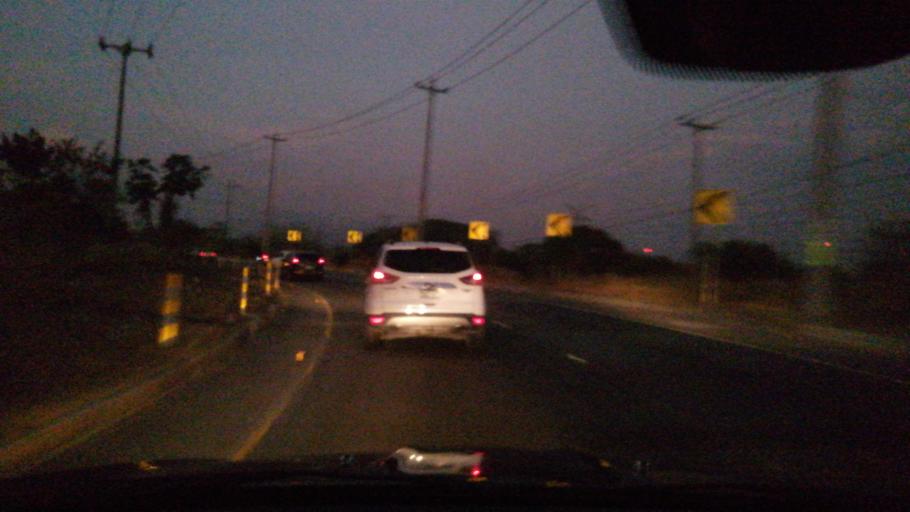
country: SV
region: San Salvador
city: Ayutuxtepeque
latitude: 13.7766
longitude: -89.2050
